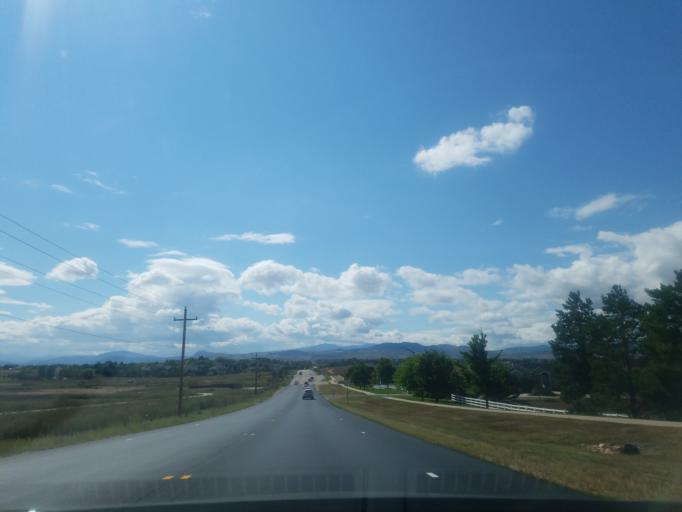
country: US
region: Colorado
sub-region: Larimer County
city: Loveland
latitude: 40.4801
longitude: -105.0541
